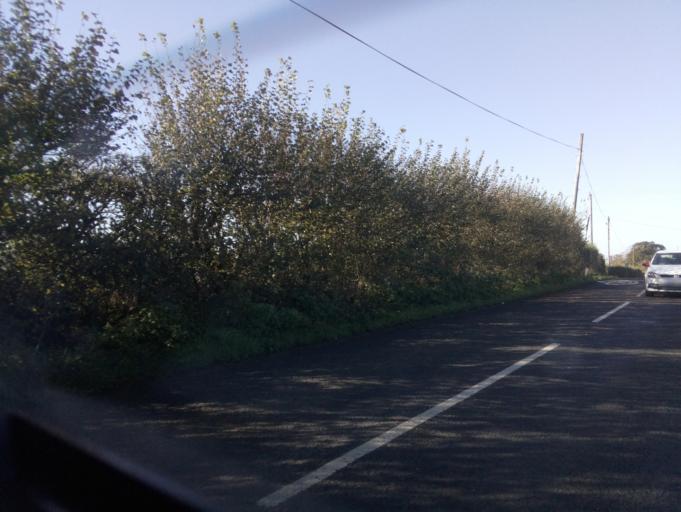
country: GB
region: England
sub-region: Somerset
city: Ilchester
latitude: 50.9710
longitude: -2.7068
